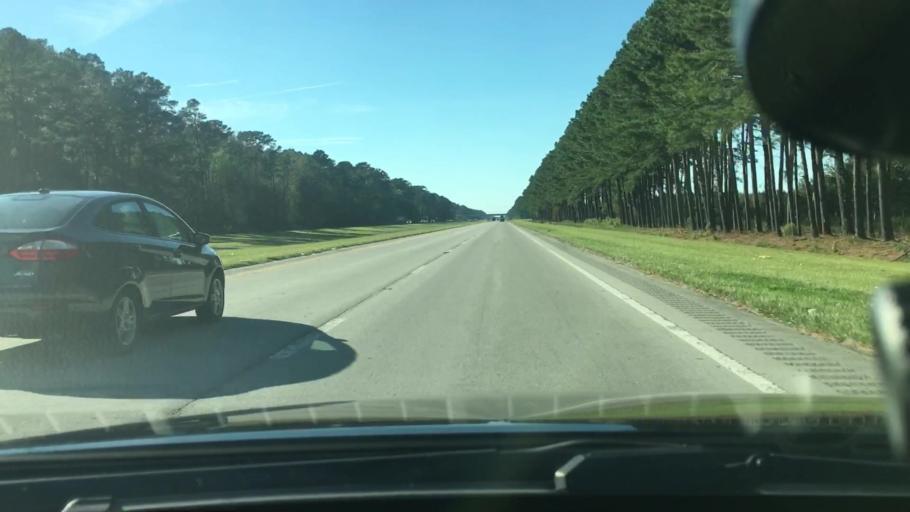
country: US
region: North Carolina
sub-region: Craven County
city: Trent Woods
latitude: 35.1231
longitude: -77.1205
